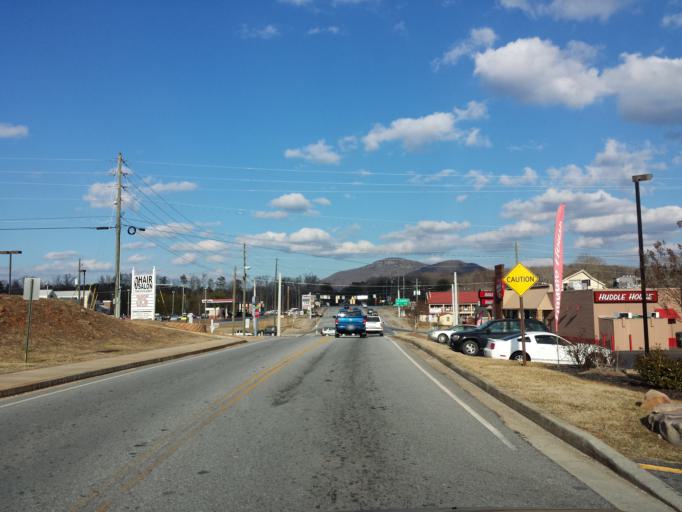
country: US
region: Georgia
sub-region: White County
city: Cleveland
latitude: 34.6011
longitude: -83.7662
